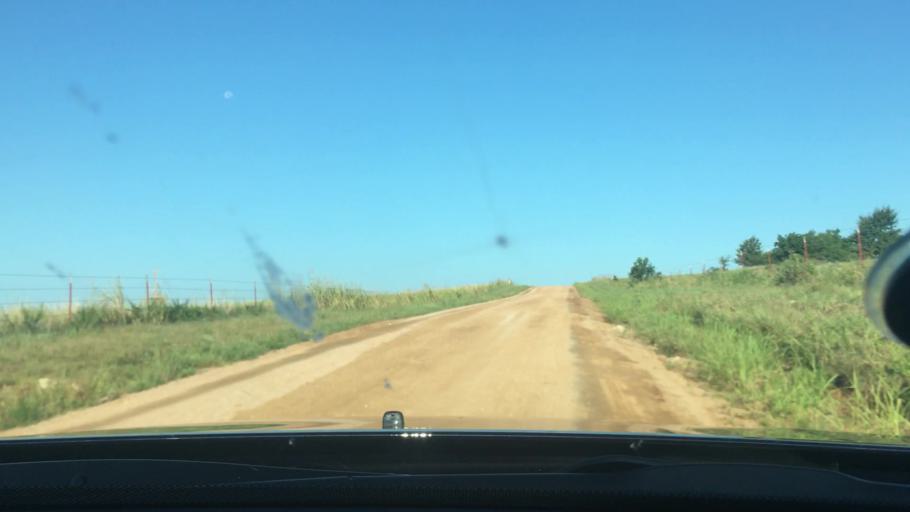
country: US
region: Oklahoma
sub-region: Johnston County
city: Tishomingo
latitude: 34.4195
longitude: -96.7731
